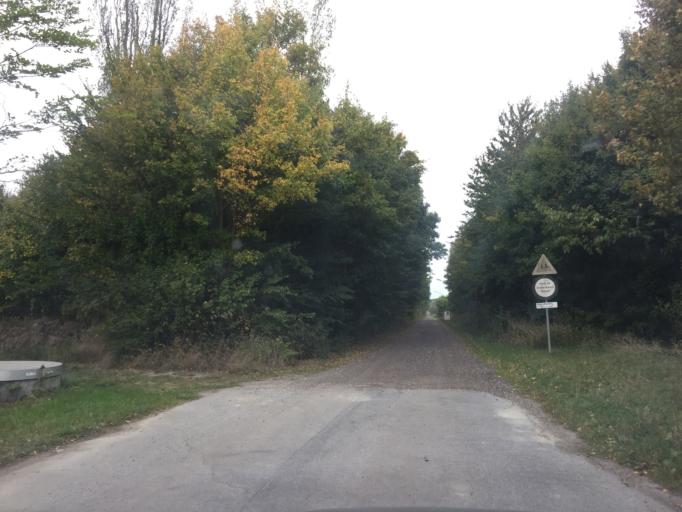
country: DK
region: Zealand
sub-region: Lolland Kommune
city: Rodbyhavn
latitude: 54.6642
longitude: 11.3518
